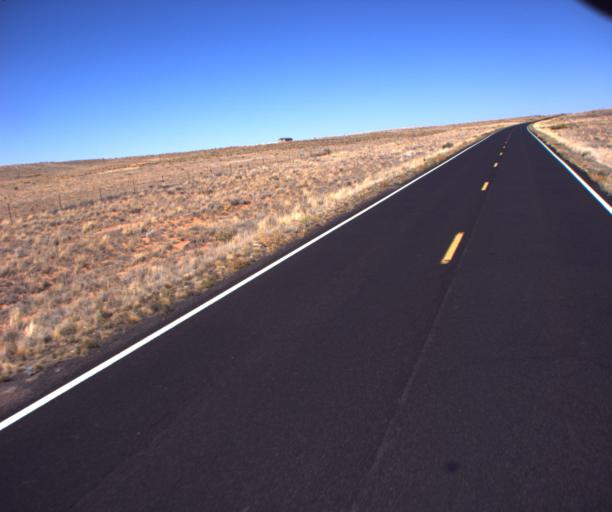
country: US
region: Arizona
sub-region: Navajo County
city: Dilkon
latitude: 35.2776
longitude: -110.4290
